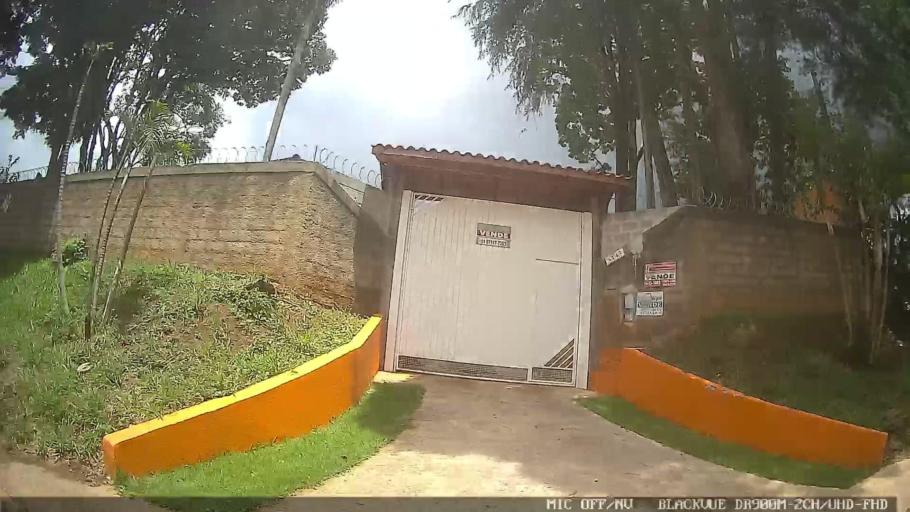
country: BR
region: Sao Paulo
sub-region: Atibaia
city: Atibaia
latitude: -23.1569
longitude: -46.5959
